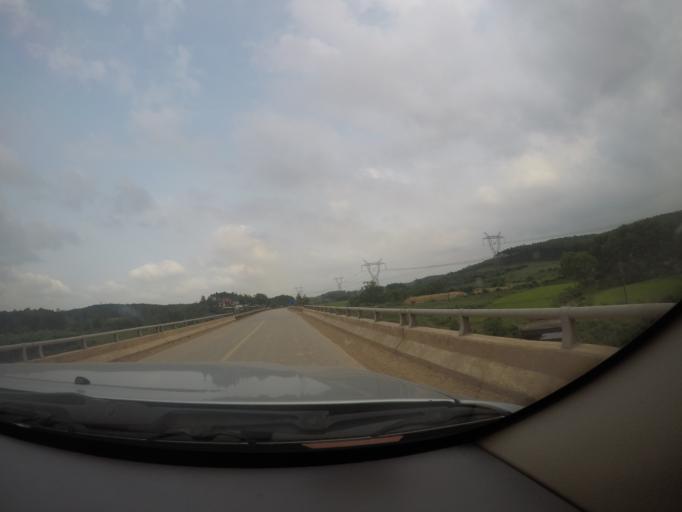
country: VN
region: Quang Binh
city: Kien Giang
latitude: 17.1221
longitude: 106.7901
